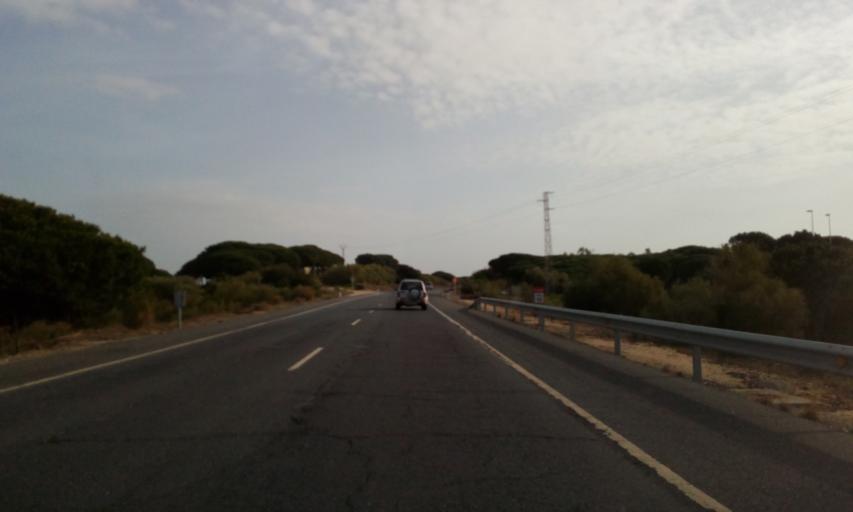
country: ES
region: Andalusia
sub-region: Provincia de Huelva
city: Palos de la Frontera
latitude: 37.1707
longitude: -6.8959
